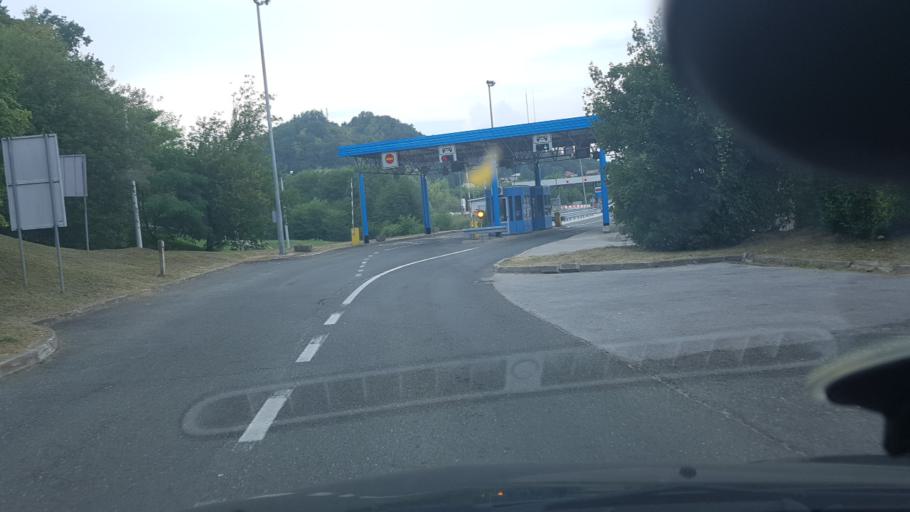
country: HR
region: Zagrebacka
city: Bregana
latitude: 45.8416
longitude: 15.6846
